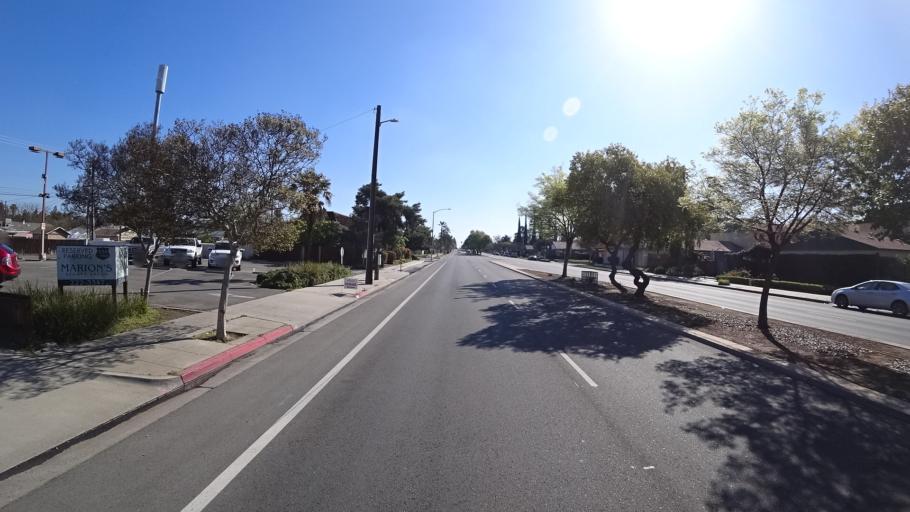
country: US
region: California
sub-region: Fresno County
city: Fresno
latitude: 36.7795
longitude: -119.8070
